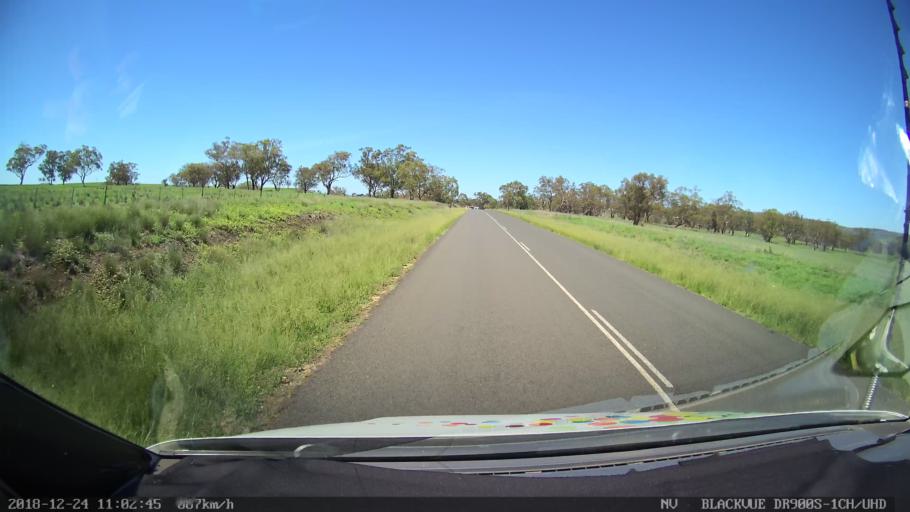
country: AU
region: New South Wales
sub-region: Upper Hunter Shire
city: Merriwa
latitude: -32.0886
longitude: 150.3724
